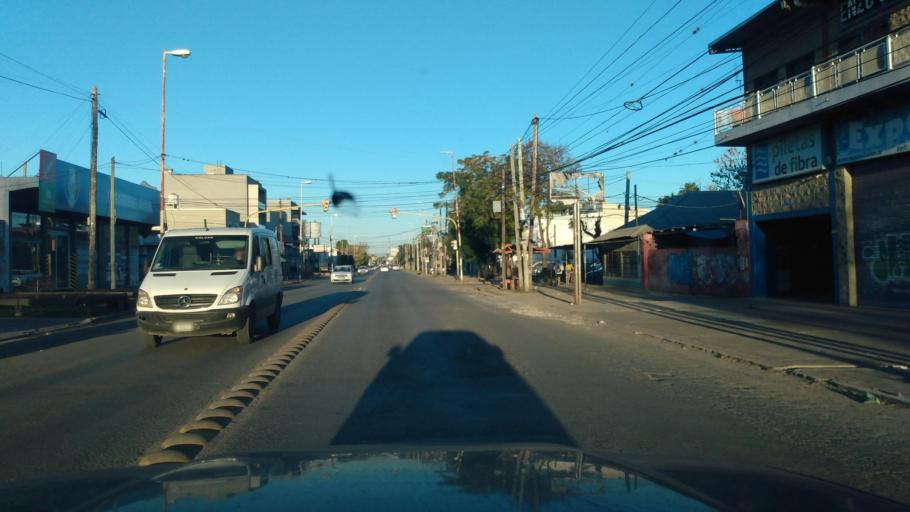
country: AR
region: Buenos Aires
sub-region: Partido de Merlo
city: Merlo
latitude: -34.6551
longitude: -58.7685
